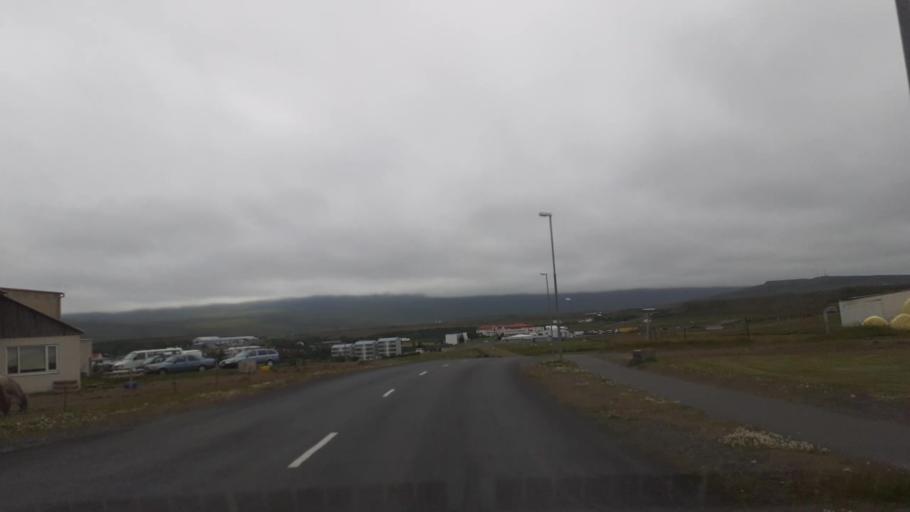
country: IS
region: Northwest
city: Saudarkrokur
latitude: 65.6570
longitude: -20.2995
